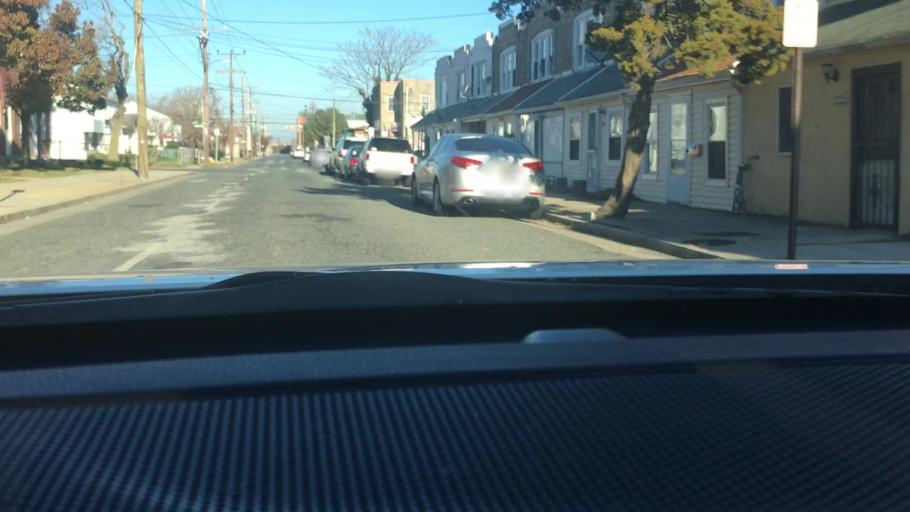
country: US
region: New Jersey
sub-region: Atlantic County
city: Atlantic City
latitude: 39.3686
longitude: -74.4340
